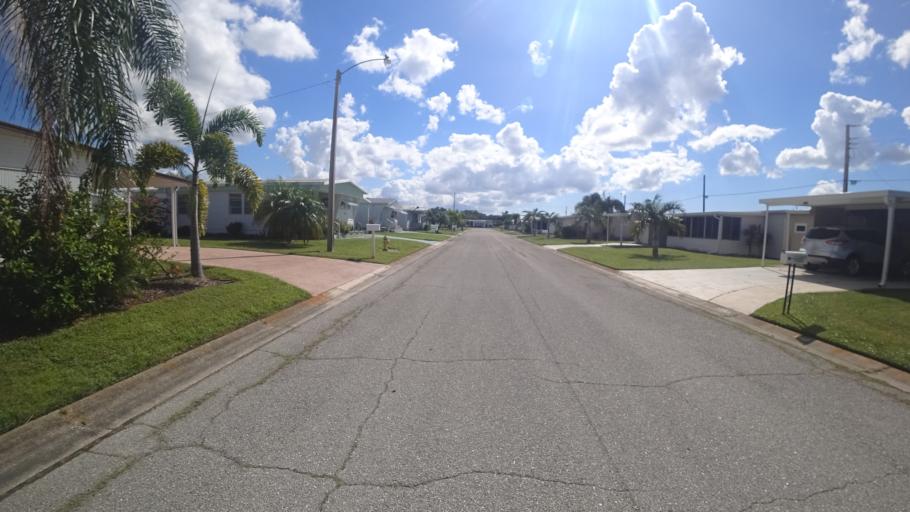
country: US
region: Florida
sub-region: Manatee County
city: Ellenton
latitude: 27.5239
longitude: -82.5198
